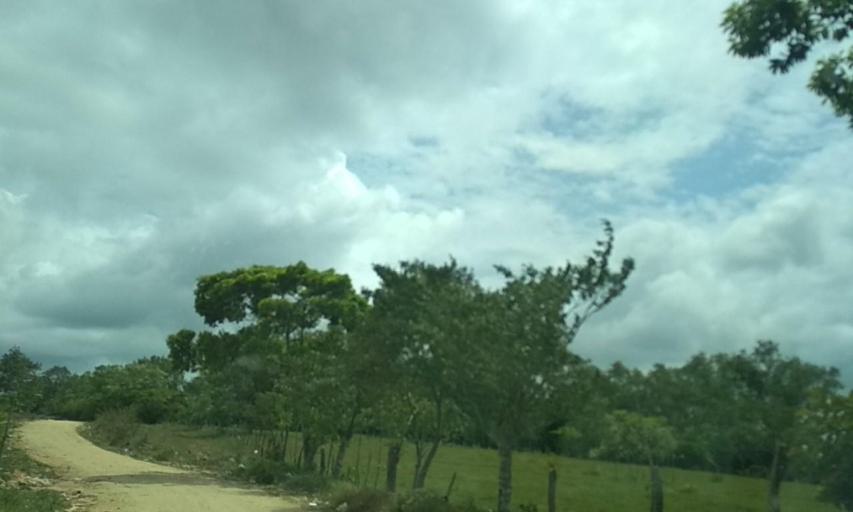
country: MX
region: Veracruz
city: Las Choapas
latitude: 17.9067
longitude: -94.1256
